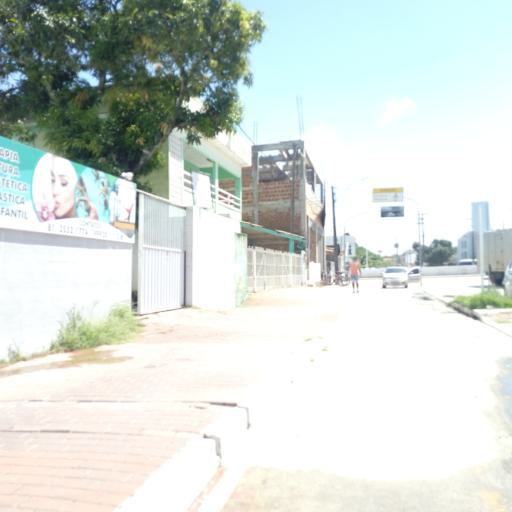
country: BR
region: Pernambuco
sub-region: Ipojuca
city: Ipojuca
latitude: -8.5056
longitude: -35.0079
